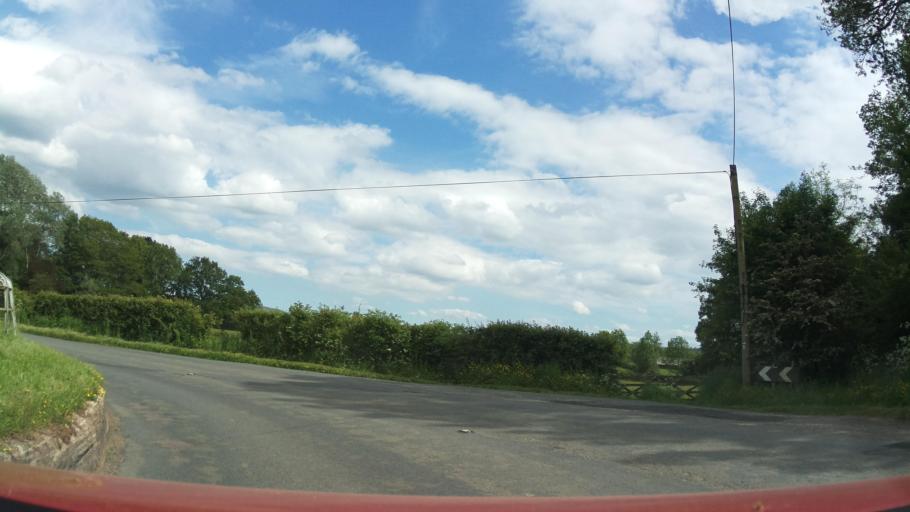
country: GB
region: England
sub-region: Herefordshire
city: Evesbatch
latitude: 52.0990
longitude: -2.4227
